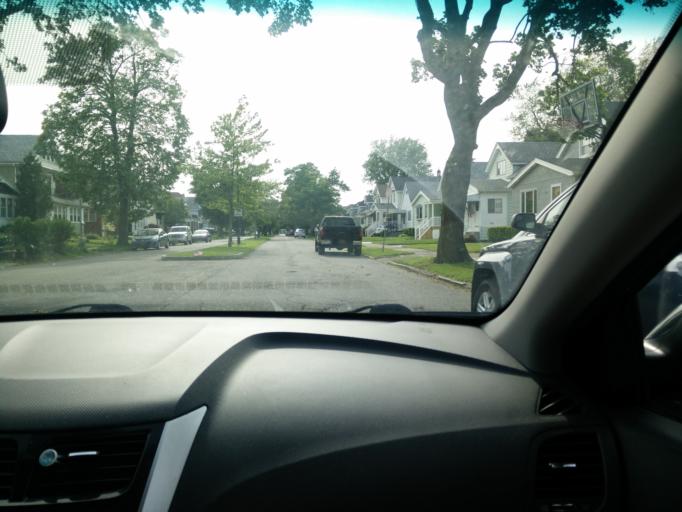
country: US
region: New York
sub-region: Erie County
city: Lackawanna
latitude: 42.8404
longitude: -78.8188
